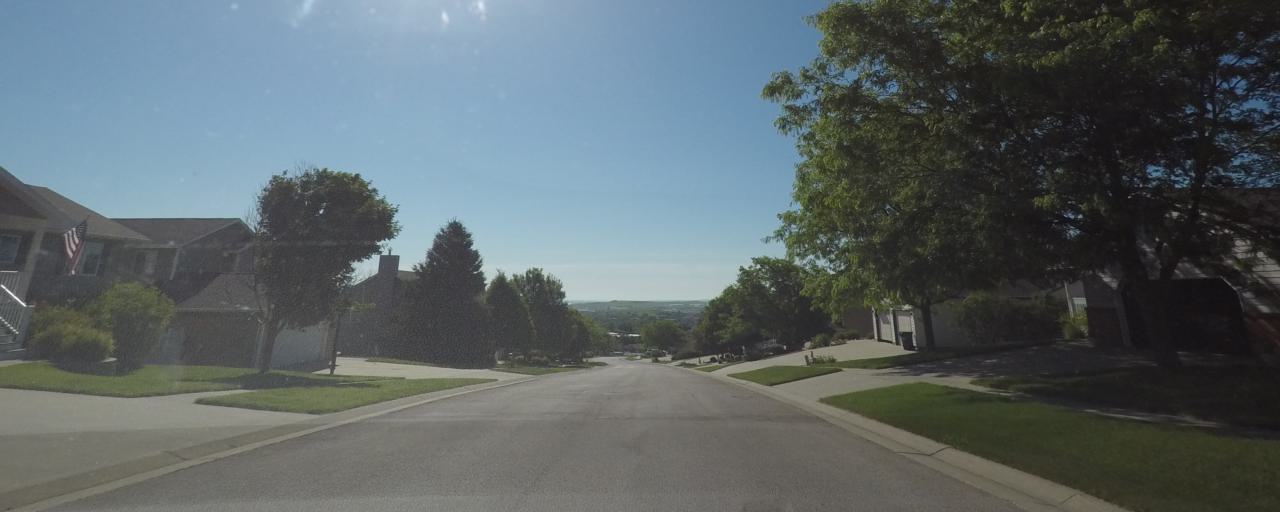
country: US
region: South Dakota
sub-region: Pennington County
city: Rapid City
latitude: 44.0513
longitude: -103.2290
